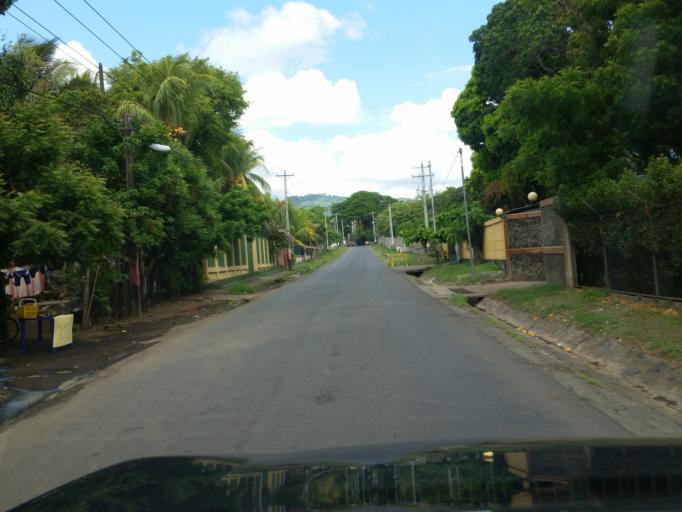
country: NI
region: Masaya
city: Ticuantepe
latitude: 12.0624
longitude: -86.1906
